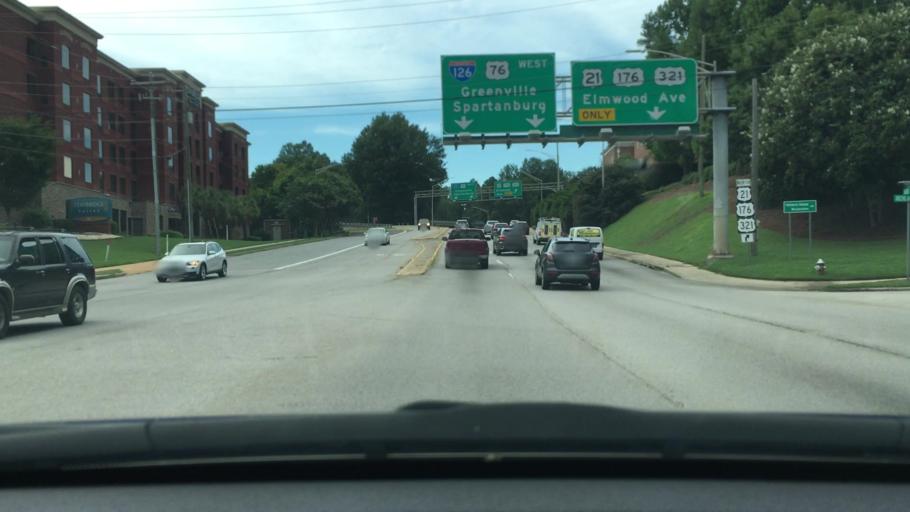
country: US
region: South Carolina
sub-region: Richland County
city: Columbia
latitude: 34.0070
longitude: -81.0490
